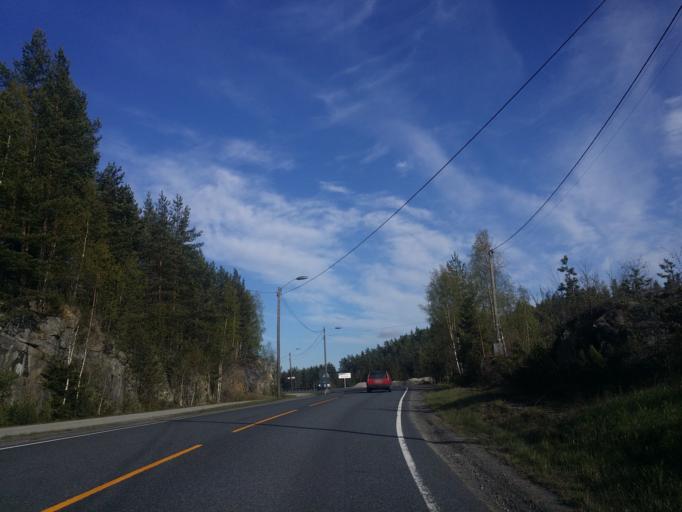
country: NO
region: Buskerud
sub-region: Kongsberg
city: Kongsberg
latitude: 59.6246
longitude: 9.6112
